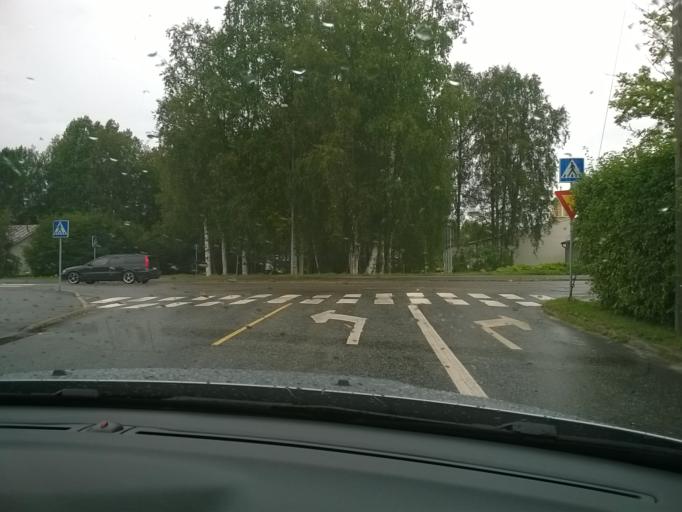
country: FI
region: Kainuu
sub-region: Kehys-Kainuu
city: Kuhmo
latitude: 64.1246
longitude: 29.5129
